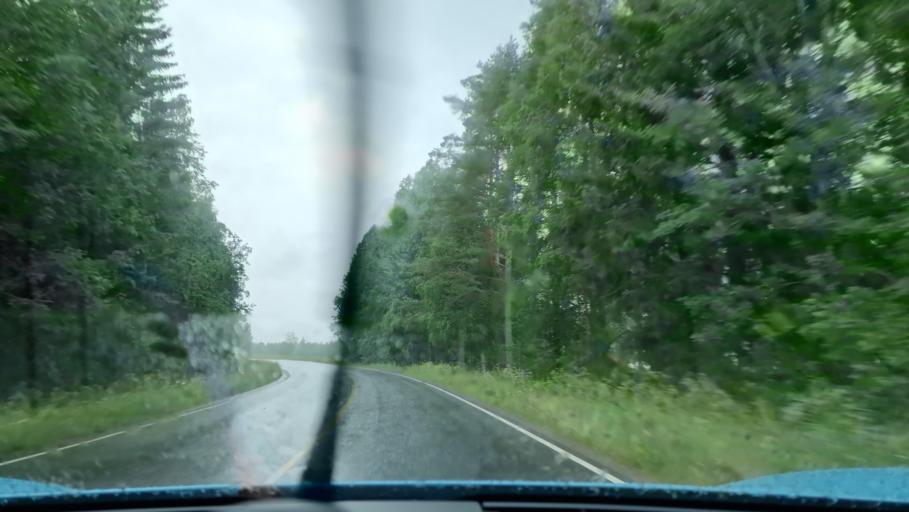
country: FI
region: Southern Ostrobothnia
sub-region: Jaerviseutu
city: Soini
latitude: 62.8279
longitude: 24.3415
